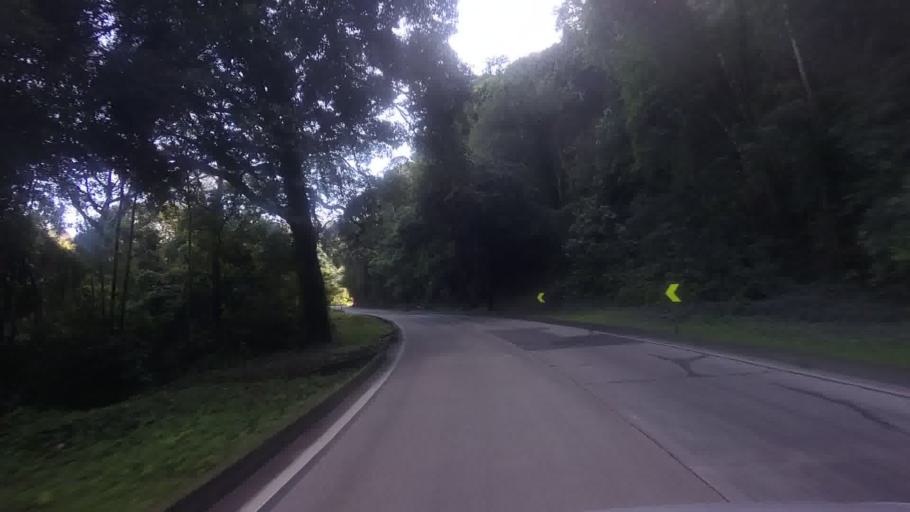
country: BR
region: Rio de Janeiro
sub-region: Petropolis
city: Petropolis
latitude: -22.5620
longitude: -43.2358
